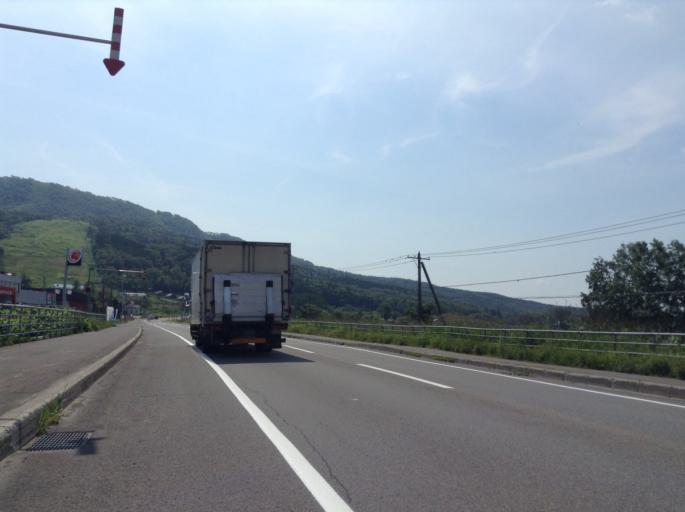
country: JP
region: Hokkaido
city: Nayoro
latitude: 44.7249
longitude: 142.2643
